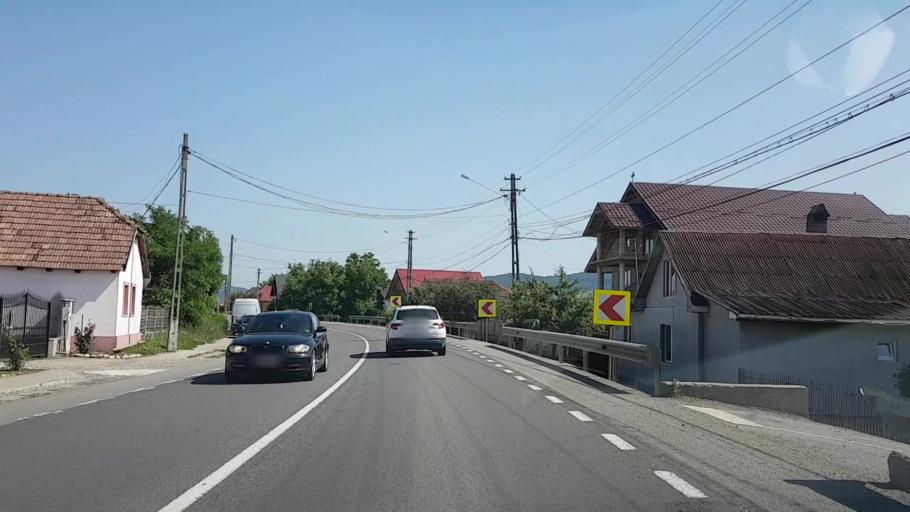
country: RO
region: Bistrita-Nasaud
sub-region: Comuna Sieu-Magherus
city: Sieu-Magherus
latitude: 47.0950
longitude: 24.3686
